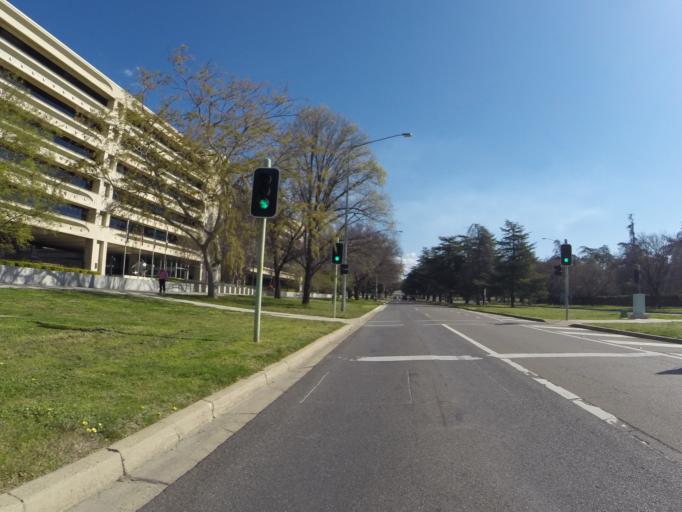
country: AU
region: Australian Capital Territory
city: Forrest
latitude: -35.3038
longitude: 149.1361
